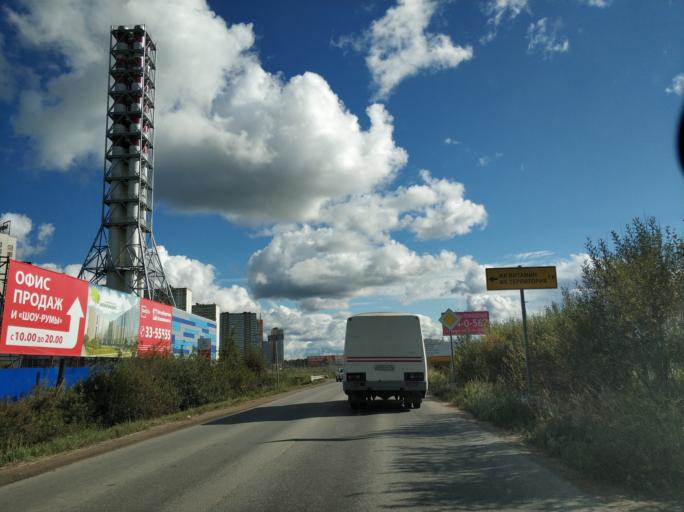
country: RU
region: St.-Petersburg
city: Grazhdanka
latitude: 60.0499
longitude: 30.4173
